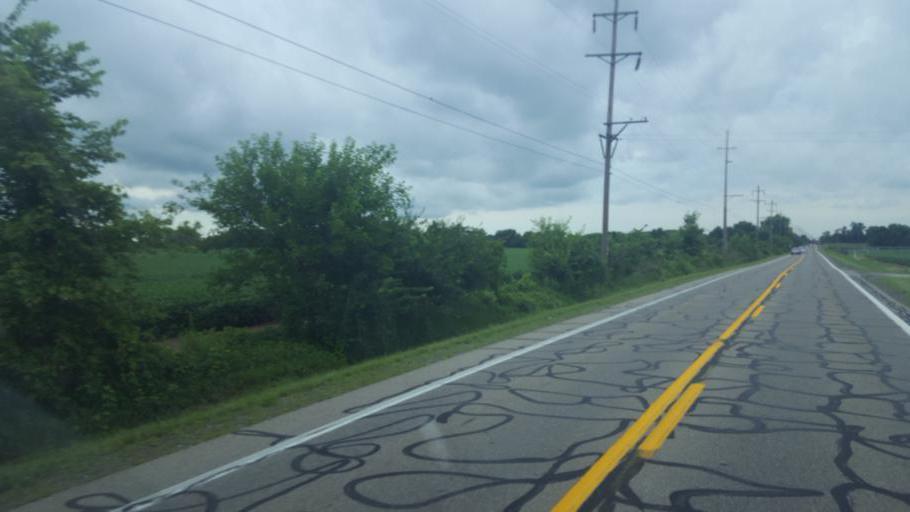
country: US
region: Ohio
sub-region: Pickaway County
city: Commercial Point
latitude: 39.7480
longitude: -83.0242
